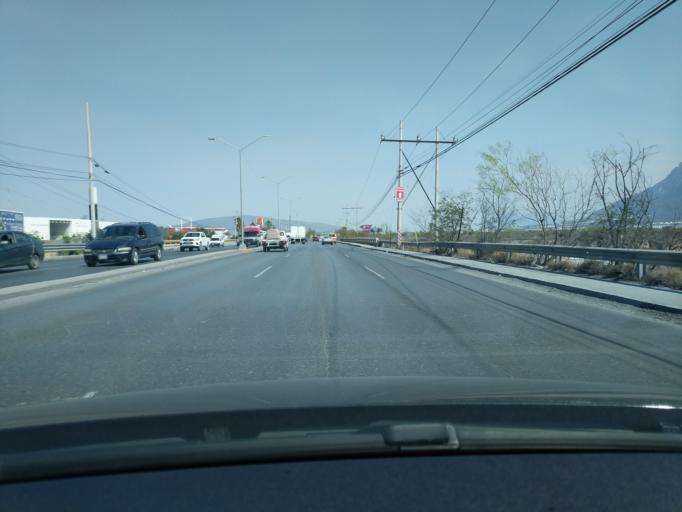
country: MX
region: Nuevo Leon
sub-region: Garcia
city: Los Parques
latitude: 25.7877
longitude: -100.4881
